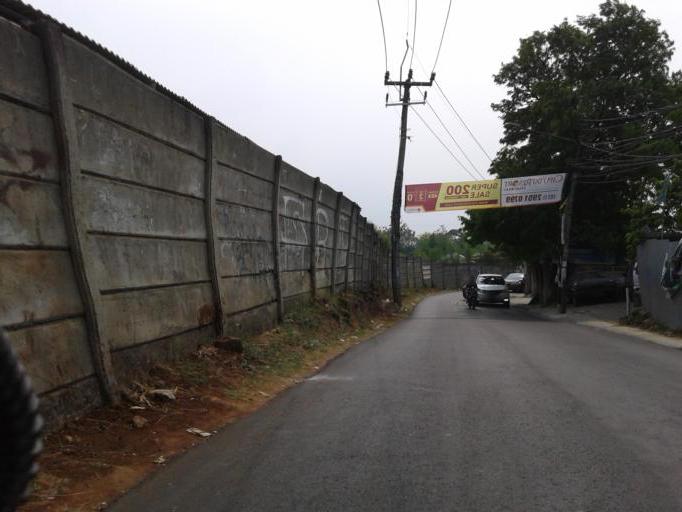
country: ID
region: Banten
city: South Tangerang
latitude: -6.2918
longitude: 106.7380
